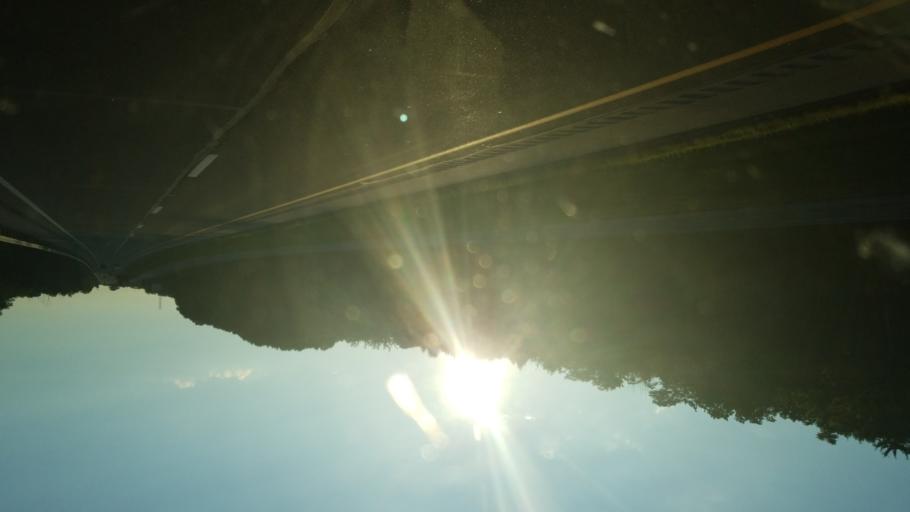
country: US
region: Ohio
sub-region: Mahoning County
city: New Middletown
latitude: 40.9299
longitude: -80.5668
